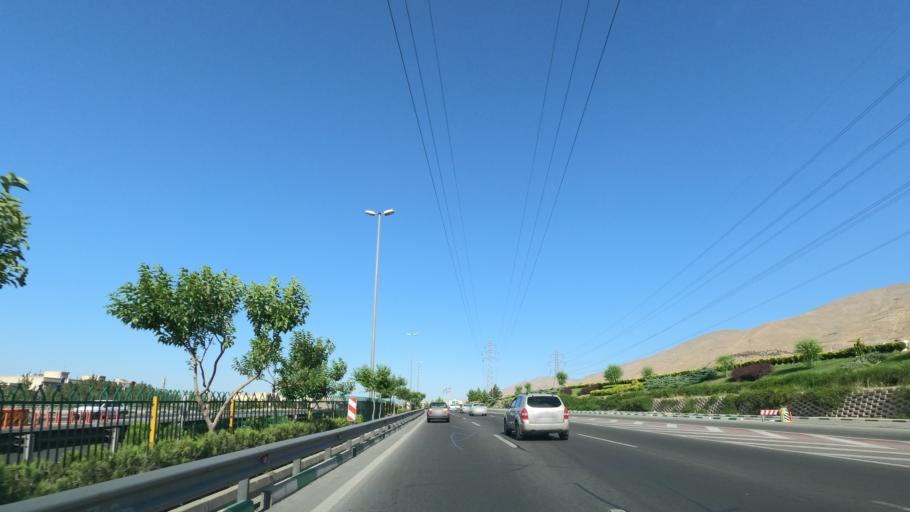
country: IR
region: Tehran
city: Shahr-e Qods
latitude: 35.7607
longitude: 51.2487
